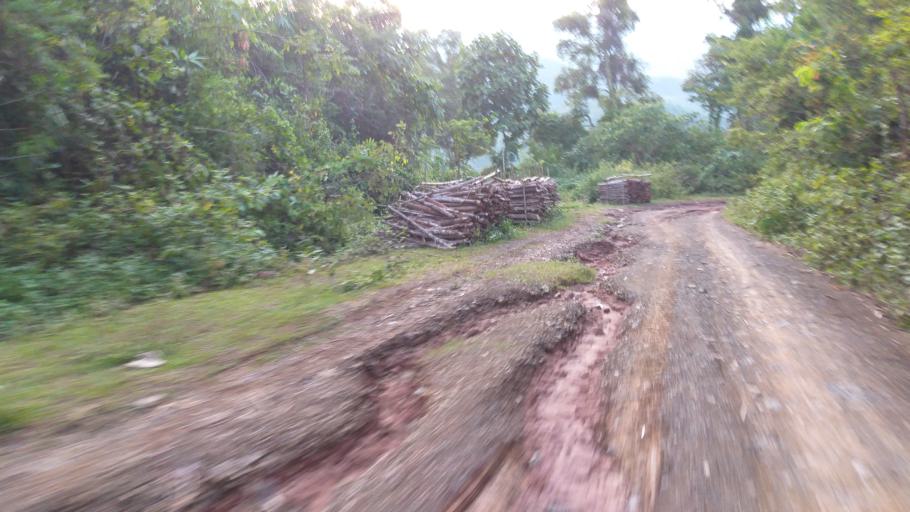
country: LA
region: Phongsali
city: Khoa
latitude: 21.4008
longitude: 102.6373
